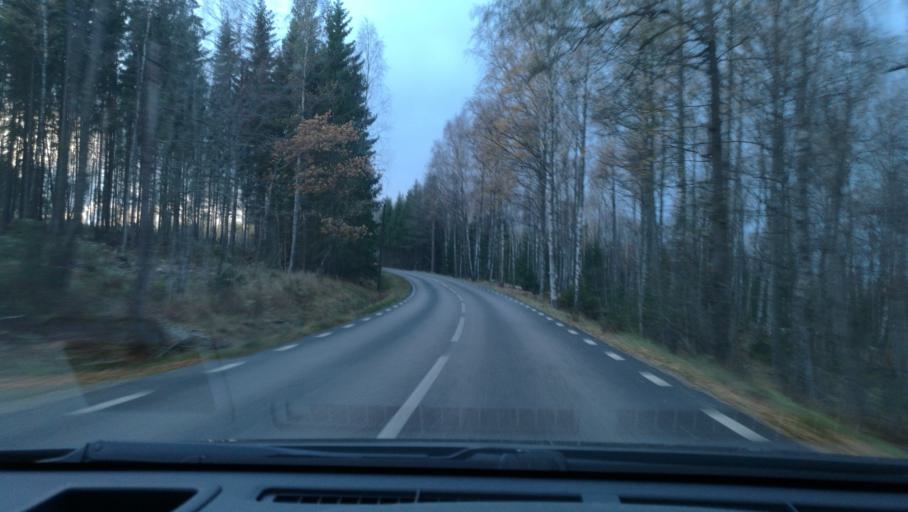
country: SE
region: Soedermanland
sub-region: Vingakers Kommun
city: Vingaker
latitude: 59.1435
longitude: 15.8704
